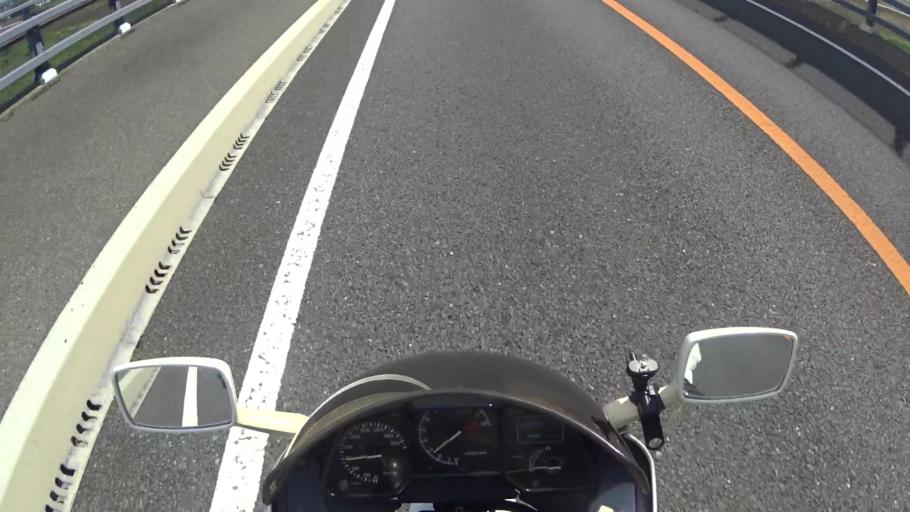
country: JP
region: Kyoto
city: Yawata
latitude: 34.8930
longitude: 135.7040
